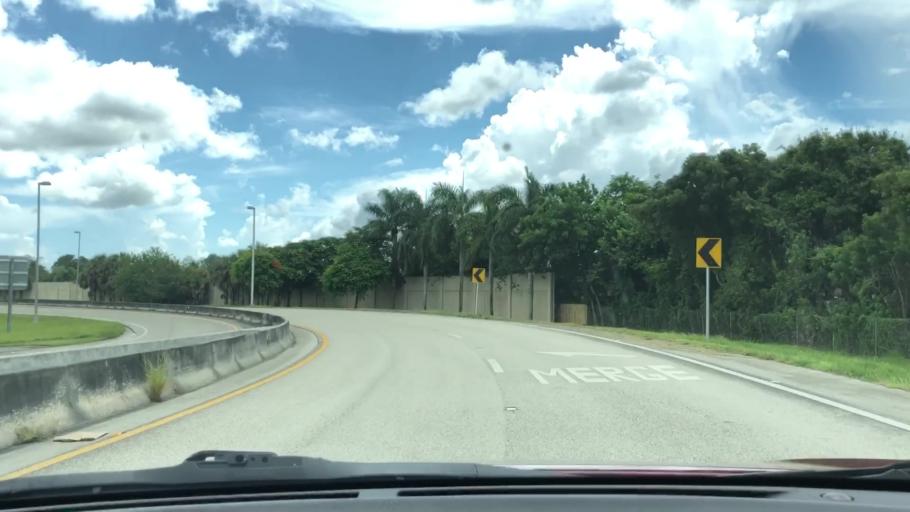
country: US
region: Florida
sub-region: Broward County
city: Parkland
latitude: 26.2980
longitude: -80.2008
